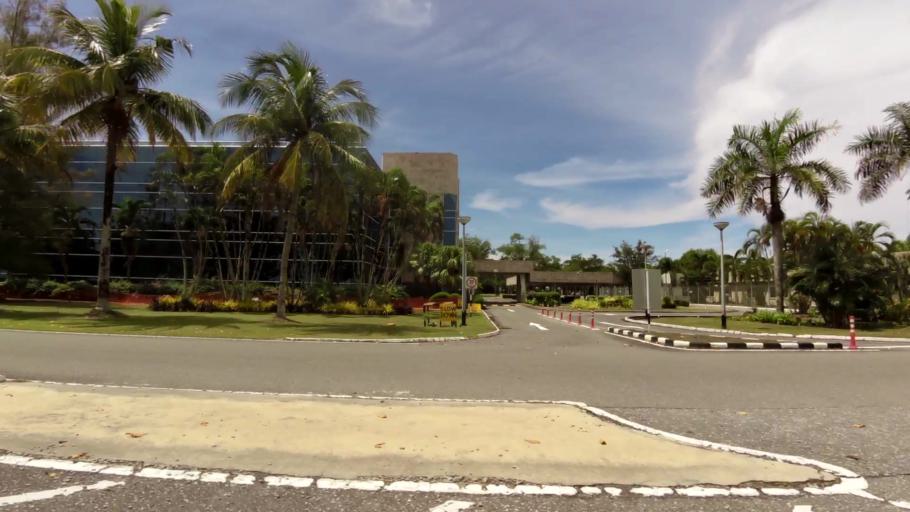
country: BN
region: Belait
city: Seria
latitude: 4.6068
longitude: 114.2915
